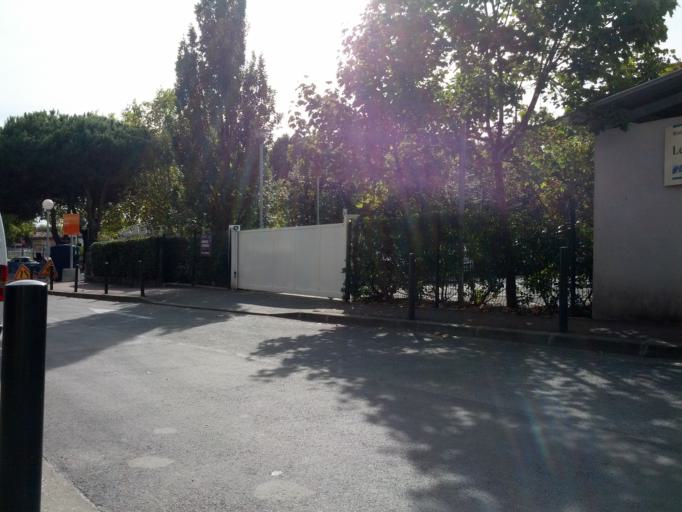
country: FR
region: Aquitaine
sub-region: Departement de la Gironde
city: Begles
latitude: 44.8075
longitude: -0.5475
